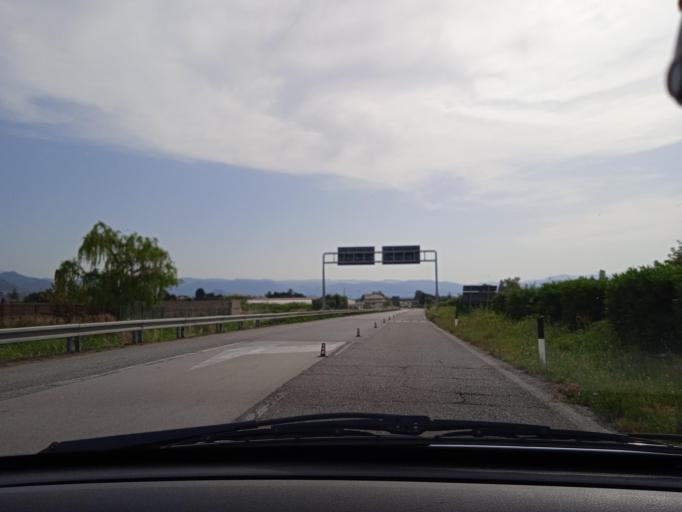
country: IT
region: Sicily
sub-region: Messina
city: Barcellona Pozzo di Gotto
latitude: 38.1545
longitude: 15.1850
